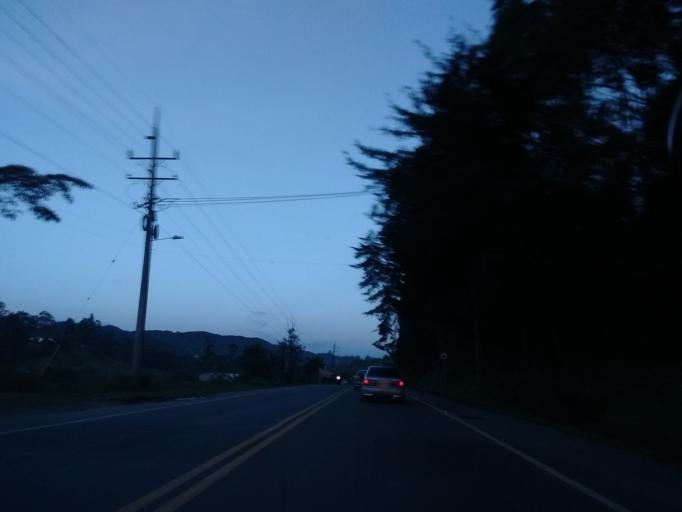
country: CO
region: Antioquia
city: Santuario
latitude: 6.1335
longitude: -75.2618
